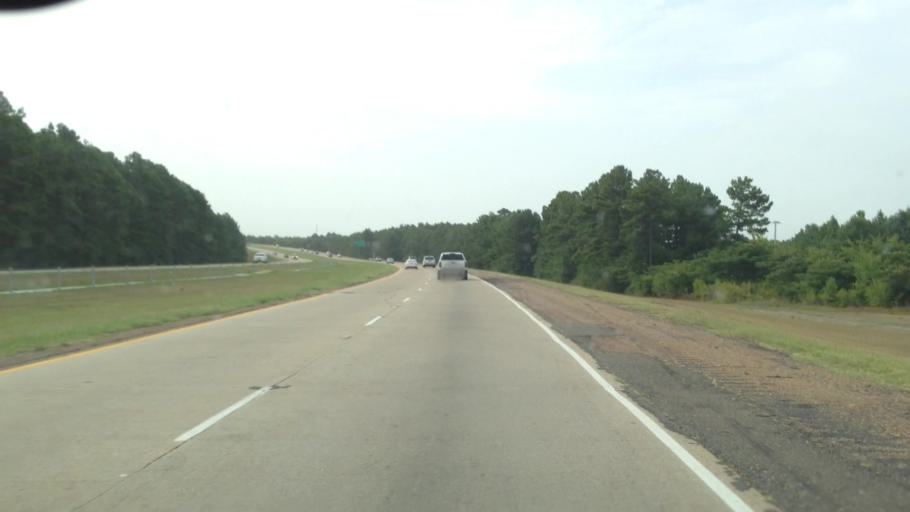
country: US
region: Louisiana
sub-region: Caddo Parish
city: Shreveport
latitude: 32.4246
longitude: -93.8372
